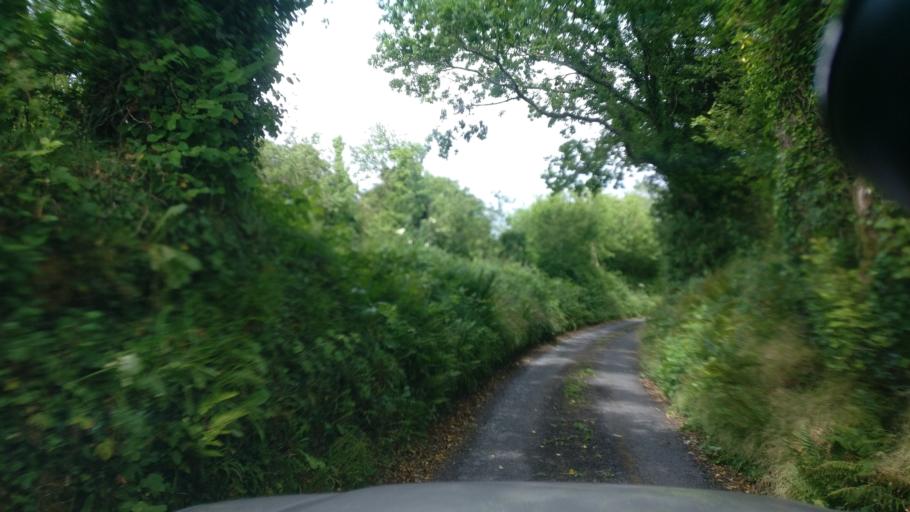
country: IE
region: Connaught
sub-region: County Galway
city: Ballinasloe
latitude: 53.2787
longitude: -8.3252
